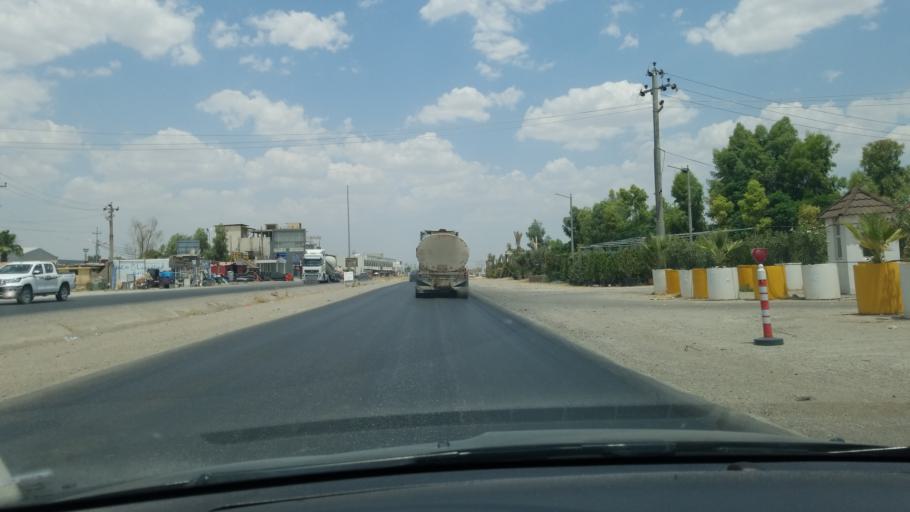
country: IQ
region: Arbil
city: Erbil
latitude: 36.1011
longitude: 44.0211
